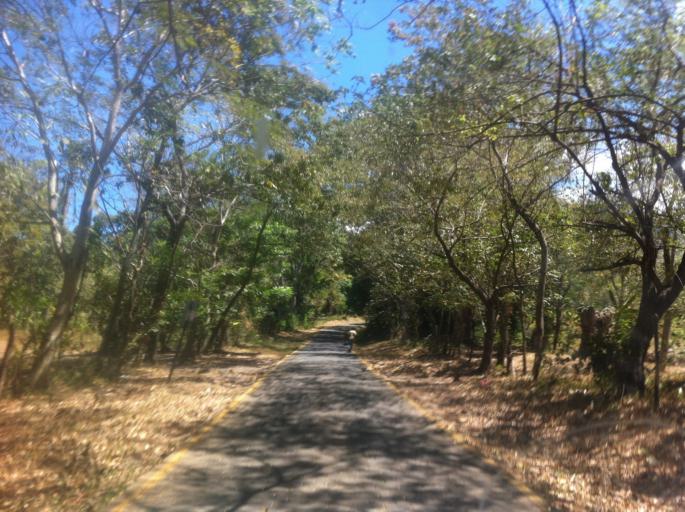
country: NI
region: Granada
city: Diriomo
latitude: 11.8411
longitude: -86.0095
